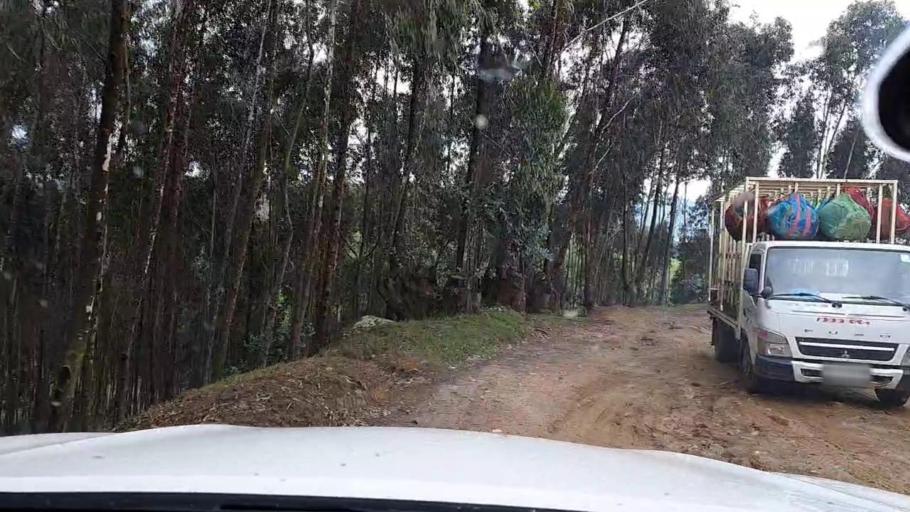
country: RW
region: Western Province
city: Kibuye
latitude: -2.2512
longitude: 29.3468
